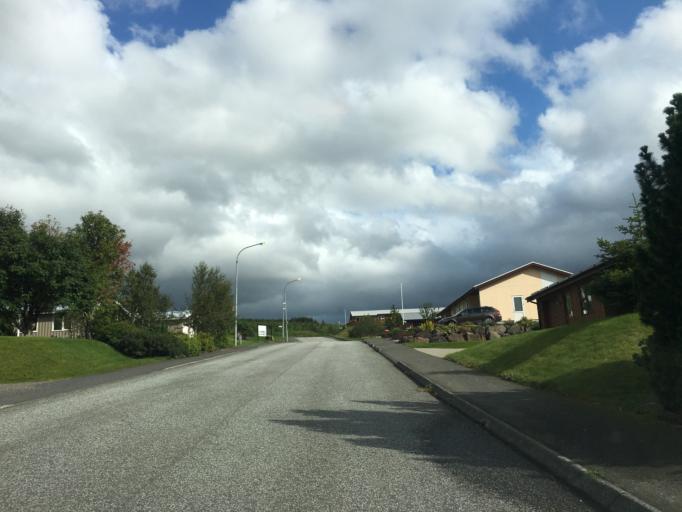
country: IS
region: East
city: Reydarfjoerdur
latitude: 65.0374
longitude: -14.2114
